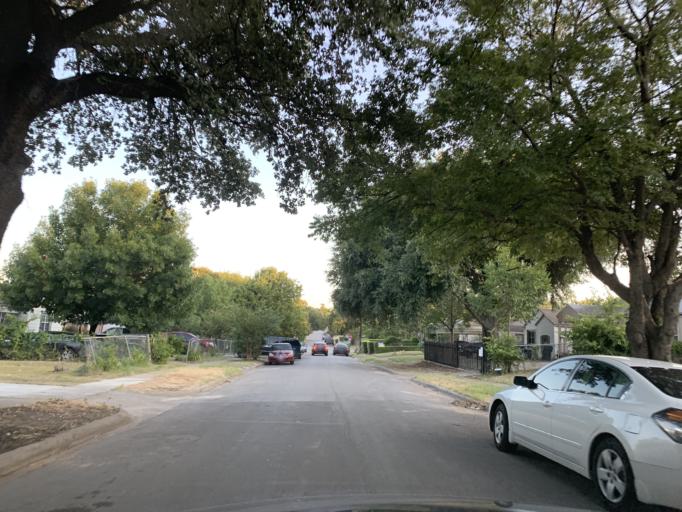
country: US
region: Texas
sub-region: Dallas County
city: Dallas
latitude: 32.7084
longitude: -96.8095
